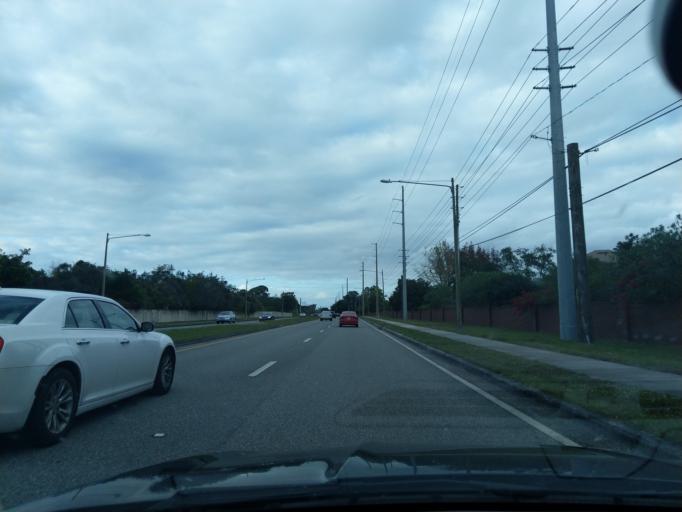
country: US
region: Florida
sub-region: Orange County
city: Doctor Phillips
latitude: 28.4177
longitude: -81.5032
